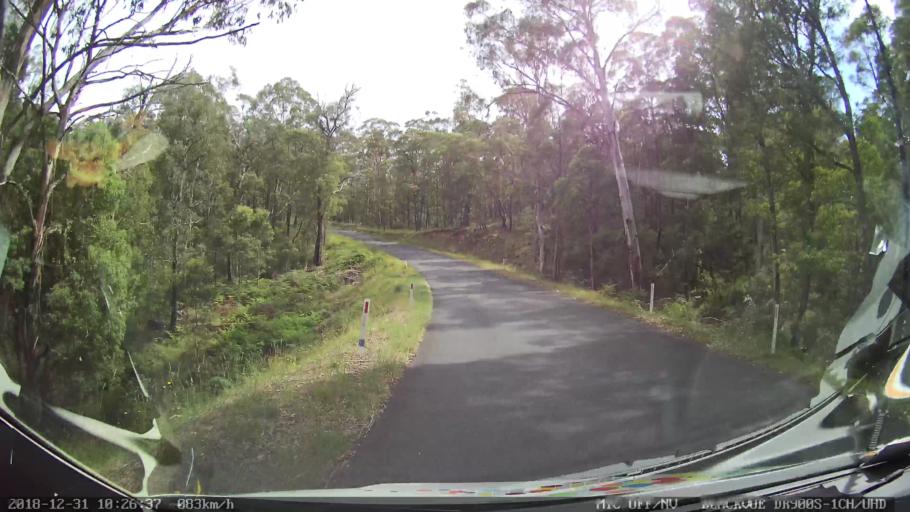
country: AU
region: New South Wales
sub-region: Snowy River
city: Jindabyne
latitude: -36.4935
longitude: 148.1407
